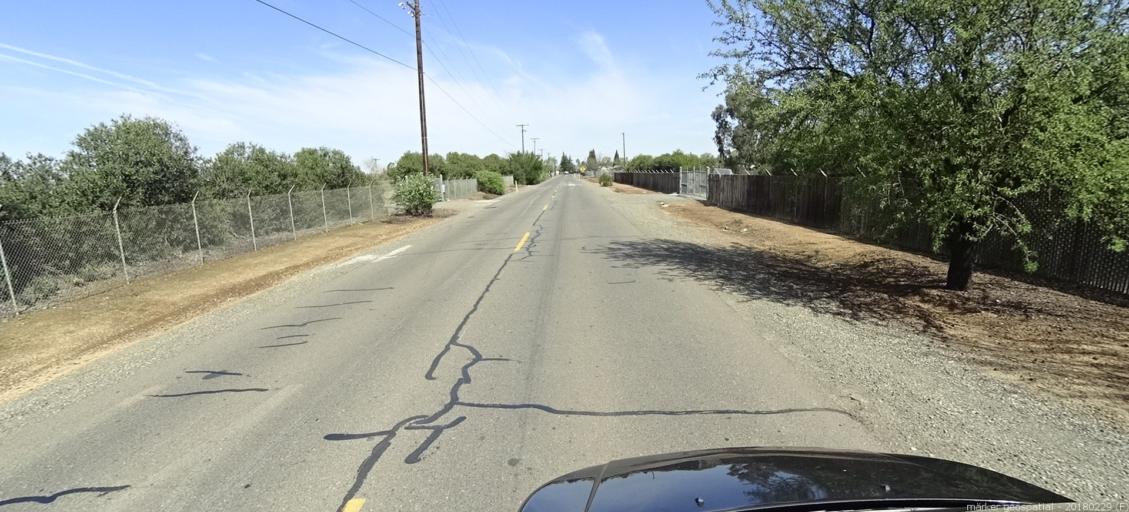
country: US
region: California
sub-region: Sacramento County
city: Rosemont
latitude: 38.5325
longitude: -121.3628
